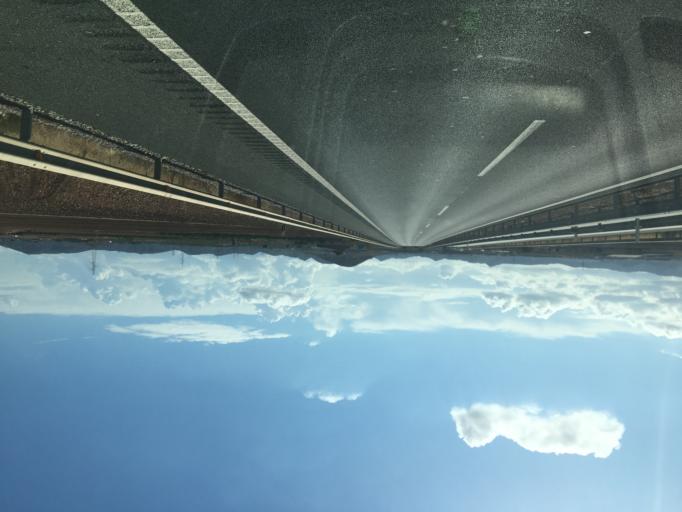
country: ES
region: Murcia
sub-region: Murcia
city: Cartagena
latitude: 37.6509
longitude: -0.9753
